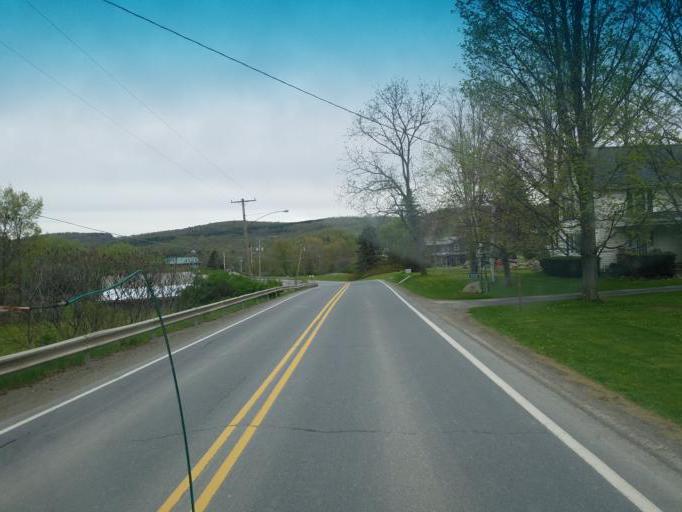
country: US
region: Pennsylvania
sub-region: Tioga County
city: Westfield
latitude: 41.8708
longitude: -77.5234
